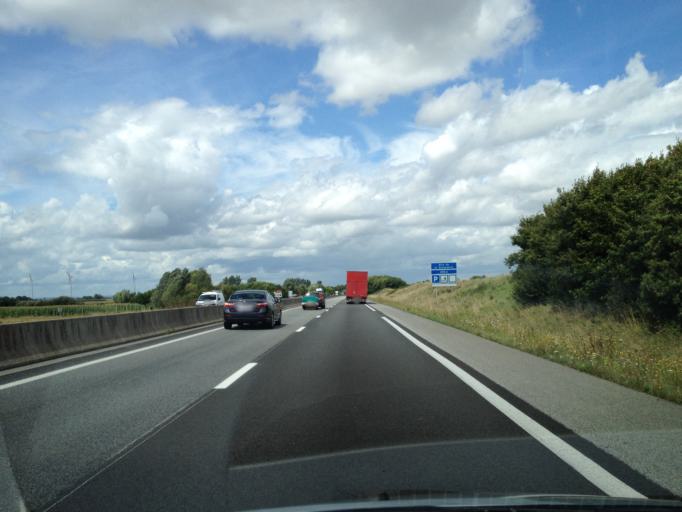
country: FR
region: Pays de la Loire
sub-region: Departement de la Sarthe
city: Beaumont-sur-Sarthe
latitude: 48.2375
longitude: 0.1680
